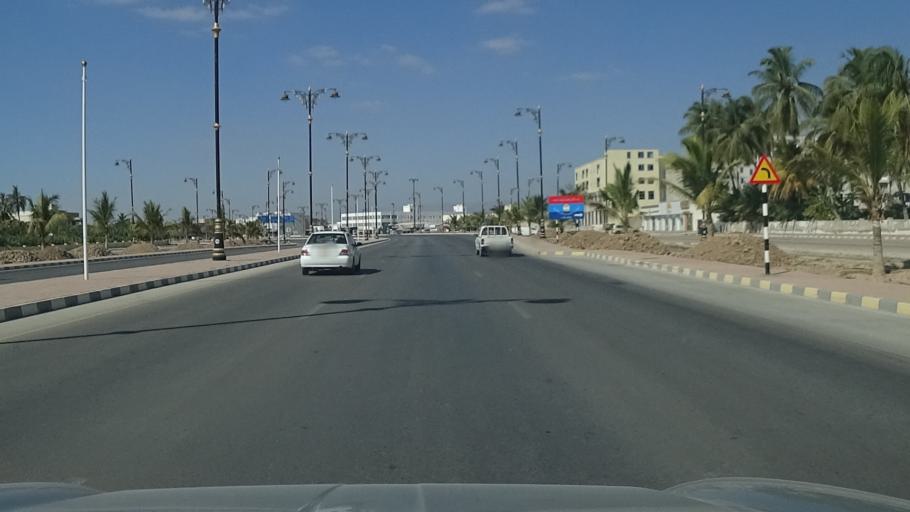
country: OM
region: Zufar
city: Salalah
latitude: 17.0366
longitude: 54.1518
